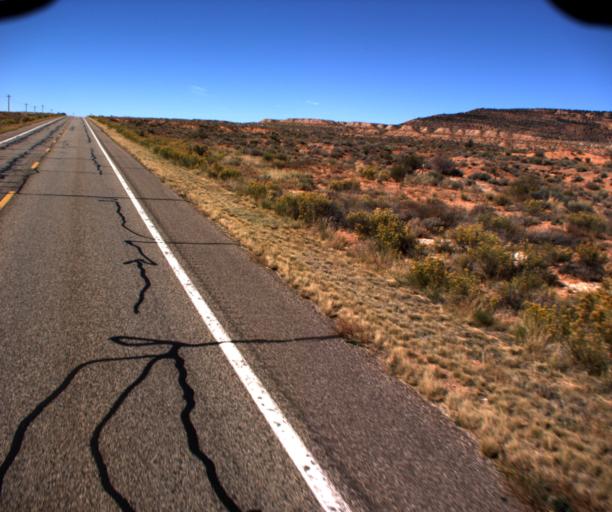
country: US
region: Arizona
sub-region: Coconino County
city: Fredonia
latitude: 36.8614
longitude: -112.7156
